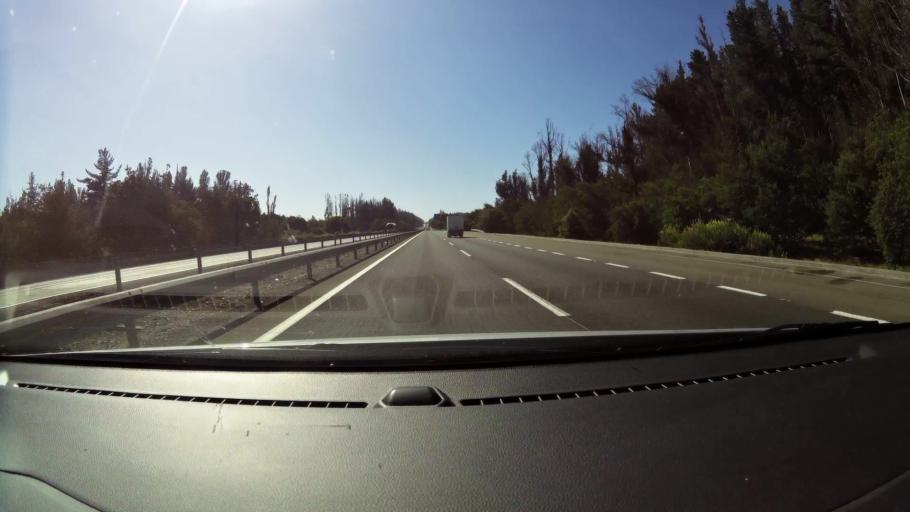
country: CL
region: Valparaiso
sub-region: Provincia de Marga Marga
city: Quilpue
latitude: -33.1749
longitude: -71.5153
